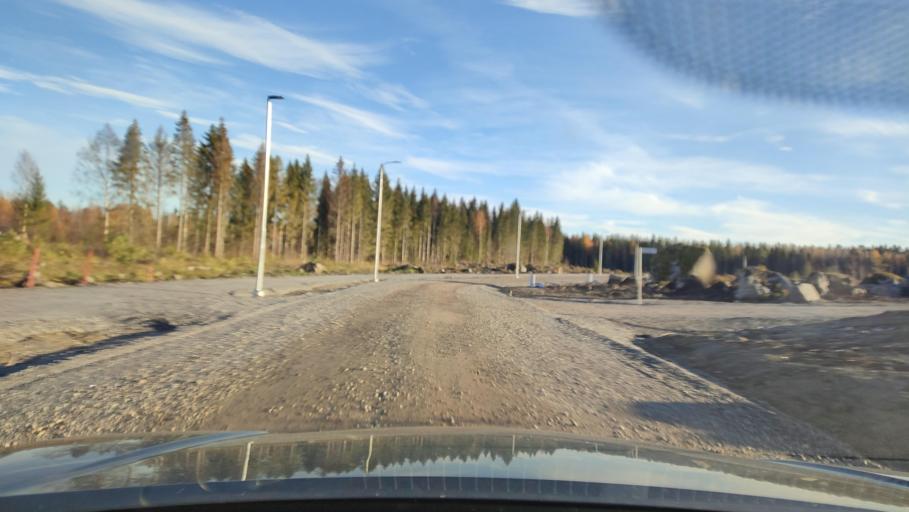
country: FI
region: Ostrobothnia
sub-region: Vaasa
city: Teeriniemi
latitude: 63.0646
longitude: 21.7013
